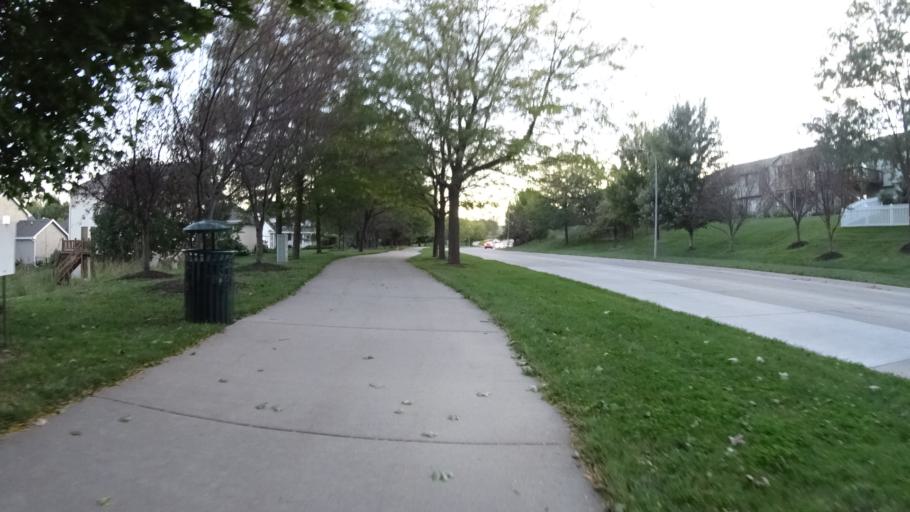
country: US
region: Nebraska
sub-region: Sarpy County
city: Papillion
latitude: 41.1351
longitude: -95.9889
